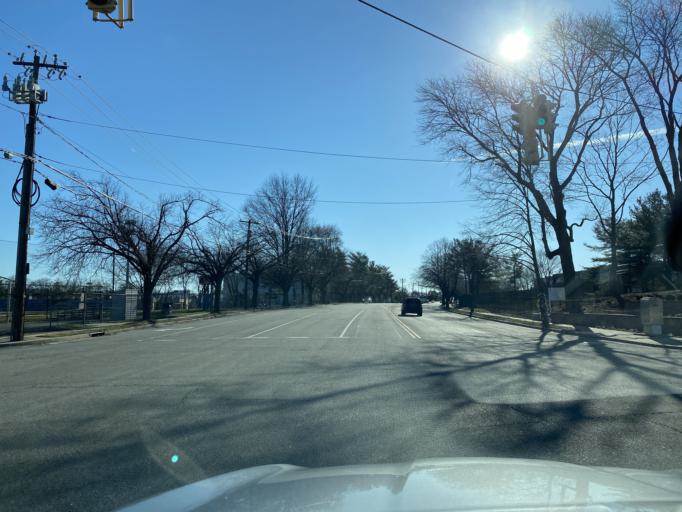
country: US
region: New York
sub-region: Nassau County
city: Manhasset Hills
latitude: 40.7580
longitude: -73.6944
